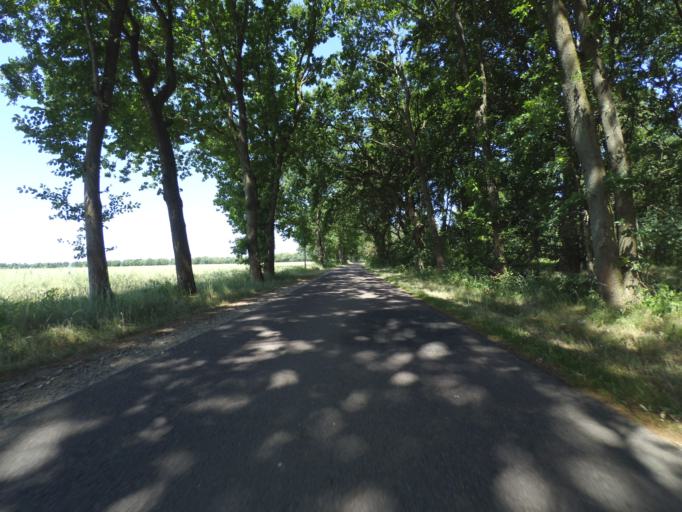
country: DE
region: Brandenburg
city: Gerdshagen
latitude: 53.2541
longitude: 12.2927
